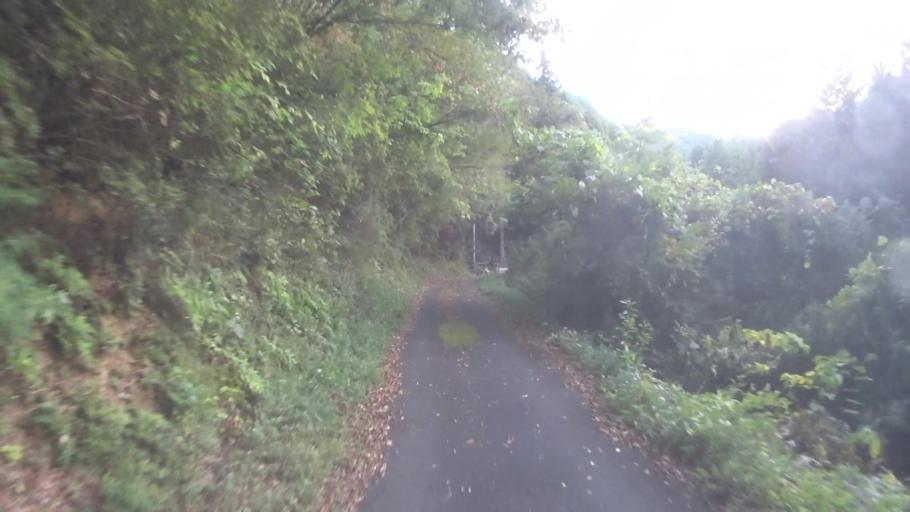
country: JP
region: Kyoto
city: Ayabe
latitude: 35.2726
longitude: 135.2491
